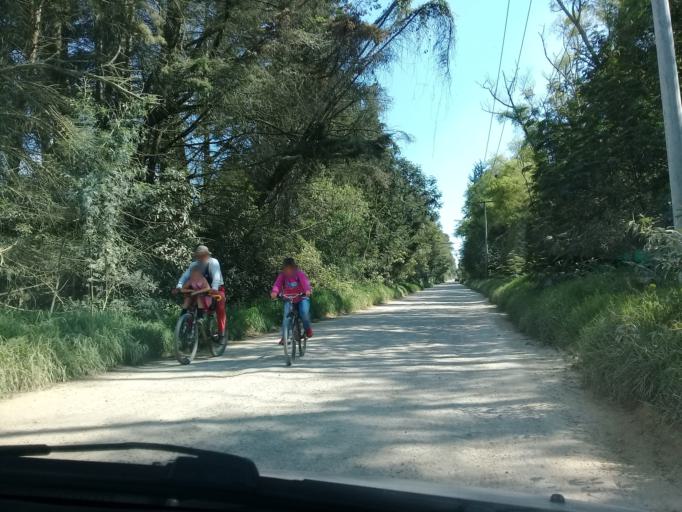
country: CO
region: Cundinamarca
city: Funza
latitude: 4.7418
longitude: -74.2014
